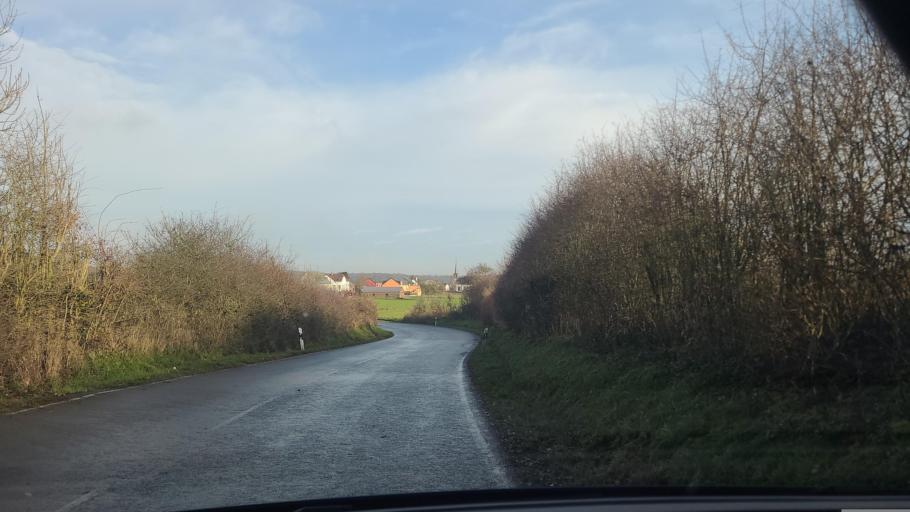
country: LU
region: Luxembourg
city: Capellen
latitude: 49.6555
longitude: 5.9739
